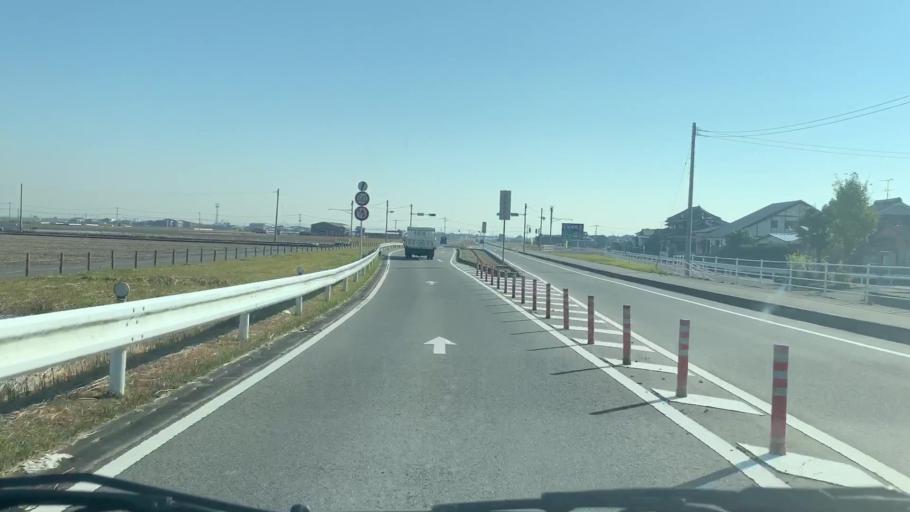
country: JP
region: Saga Prefecture
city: Saga-shi
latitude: 33.2214
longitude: 130.1961
